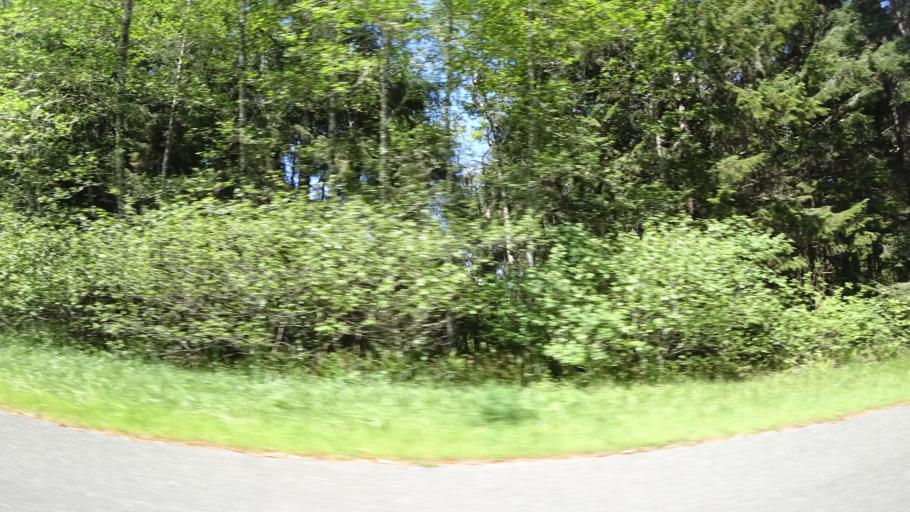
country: US
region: California
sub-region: Humboldt County
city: Westhaven-Moonstone
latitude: 41.1096
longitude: -124.1548
